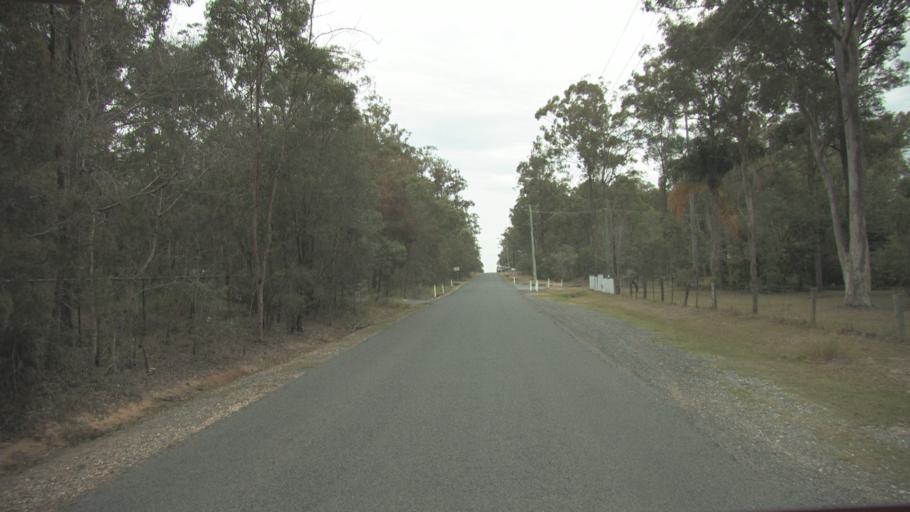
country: AU
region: Queensland
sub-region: Logan
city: Chambers Flat
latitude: -27.7936
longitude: 153.1215
